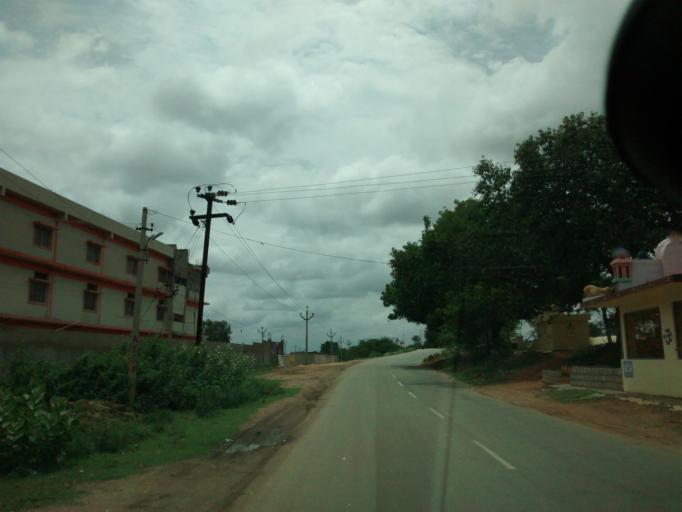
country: IN
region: Andhra Pradesh
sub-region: Anantapur
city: Hindupur
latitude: 13.8186
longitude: 77.5089
